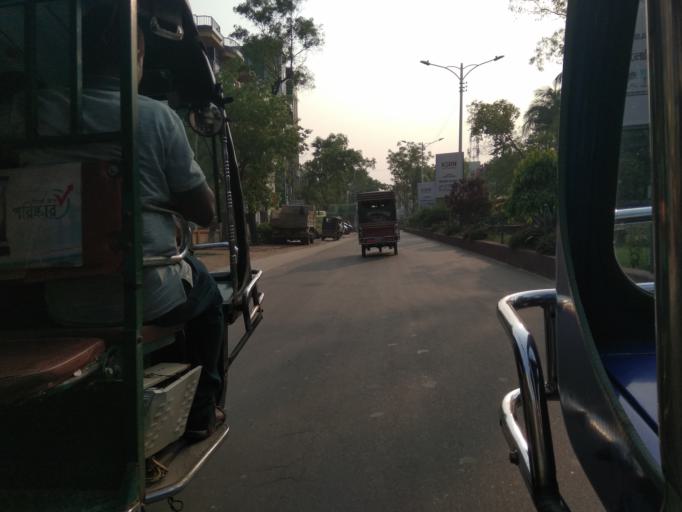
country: BD
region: Khulna
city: Khulna
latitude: 22.8194
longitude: 89.5484
